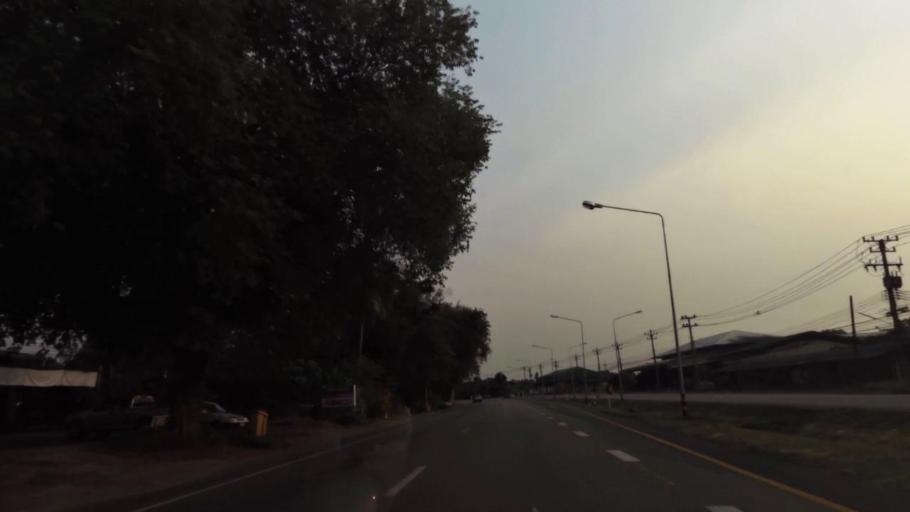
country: TH
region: Chanthaburi
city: Khlung
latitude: 12.4892
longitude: 102.1745
